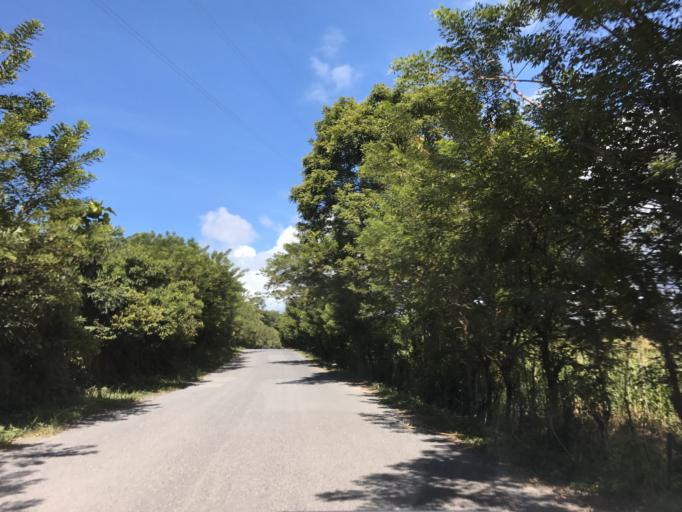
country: GT
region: Izabal
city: Morales
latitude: 15.6465
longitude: -89.0174
